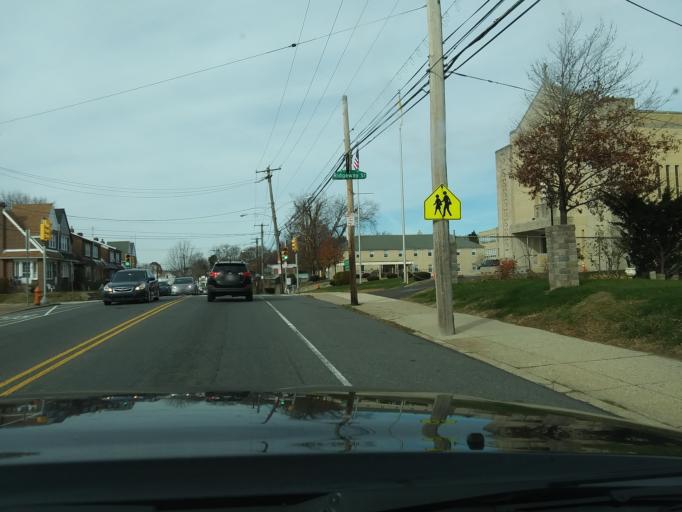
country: US
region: Pennsylvania
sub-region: Montgomery County
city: Rockledge
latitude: 40.0757
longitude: -75.0804
